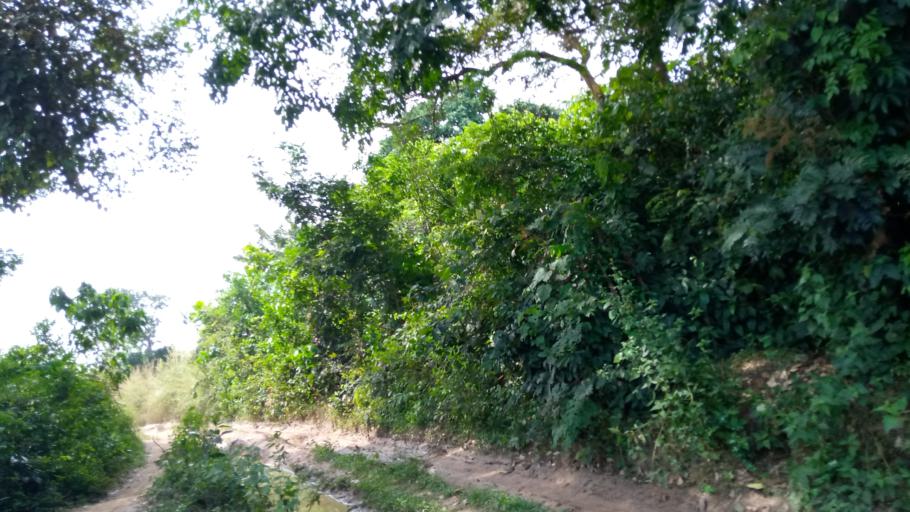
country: CD
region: Bandundu
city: Bandundu
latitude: -4.1341
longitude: 17.4159
